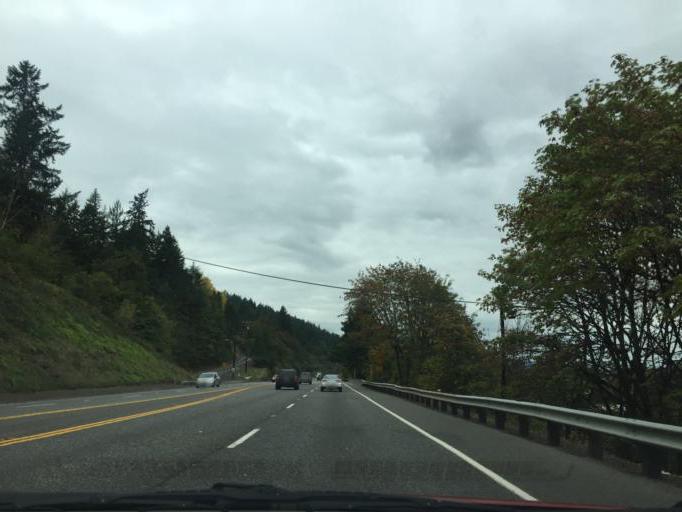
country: US
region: Oregon
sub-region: Washington County
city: Oak Hills
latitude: 45.6170
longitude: -122.8054
